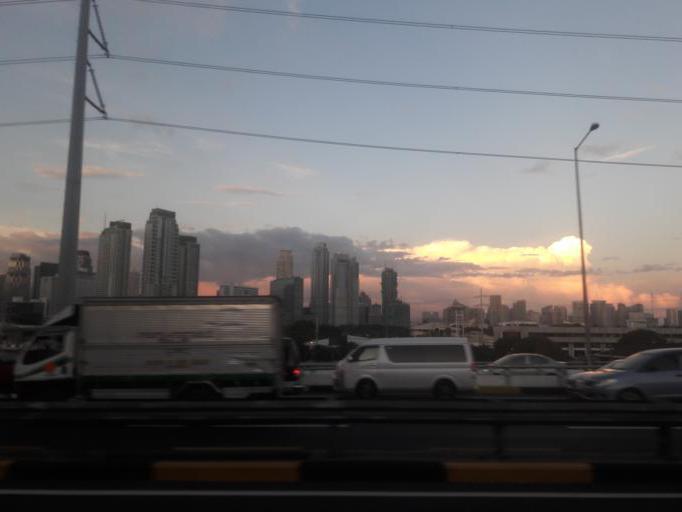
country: PH
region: Metro Manila
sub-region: Makati City
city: Makati City
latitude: 14.5450
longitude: 121.0143
